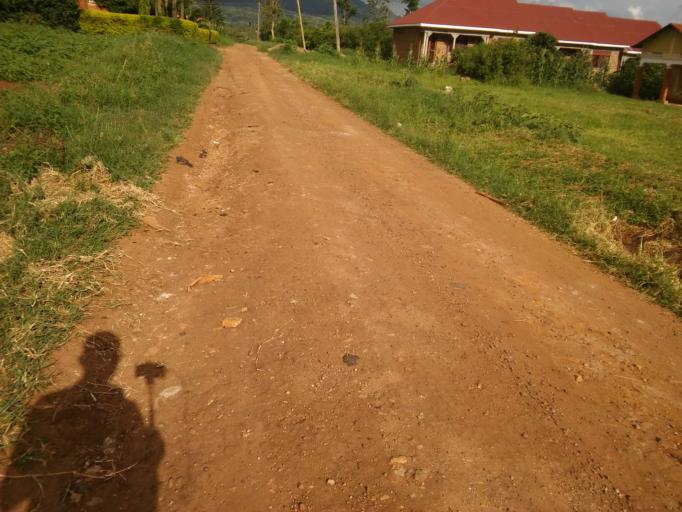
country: UG
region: Eastern Region
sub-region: Mbale District
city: Mbale
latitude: 1.0668
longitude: 34.1816
